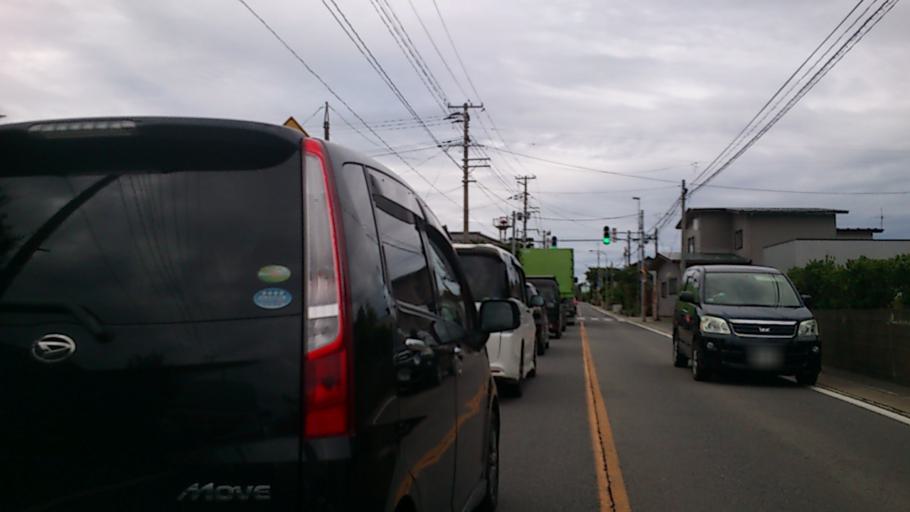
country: JP
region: Akita
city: Akita Shi
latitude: 39.6273
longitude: 140.0650
